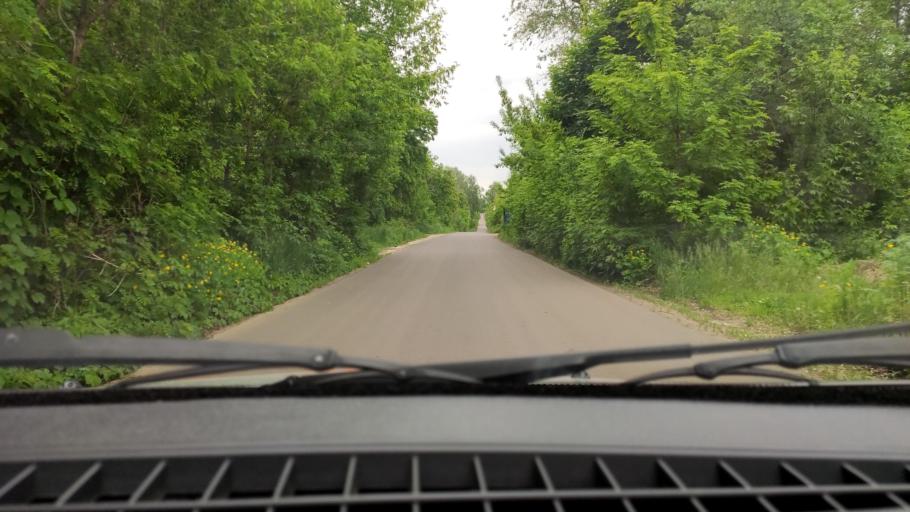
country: RU
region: Voronezj
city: Shilovo
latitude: 51.5995
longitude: 39.1324
